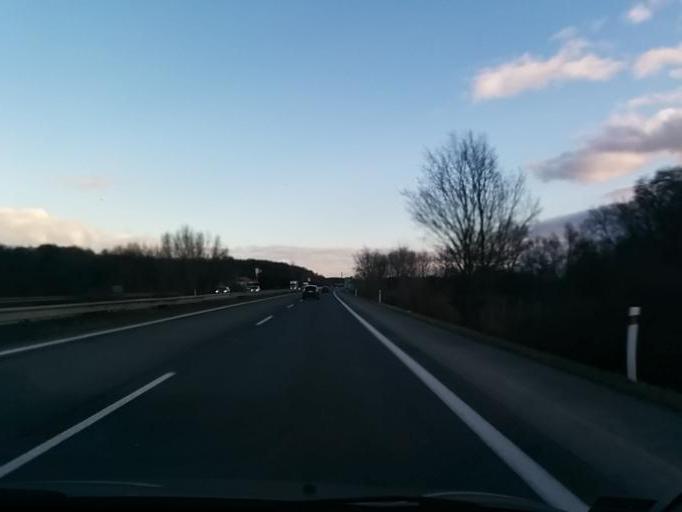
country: SK
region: Trnavsky
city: Leopoldov
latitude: 48.4491
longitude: 17.7389
